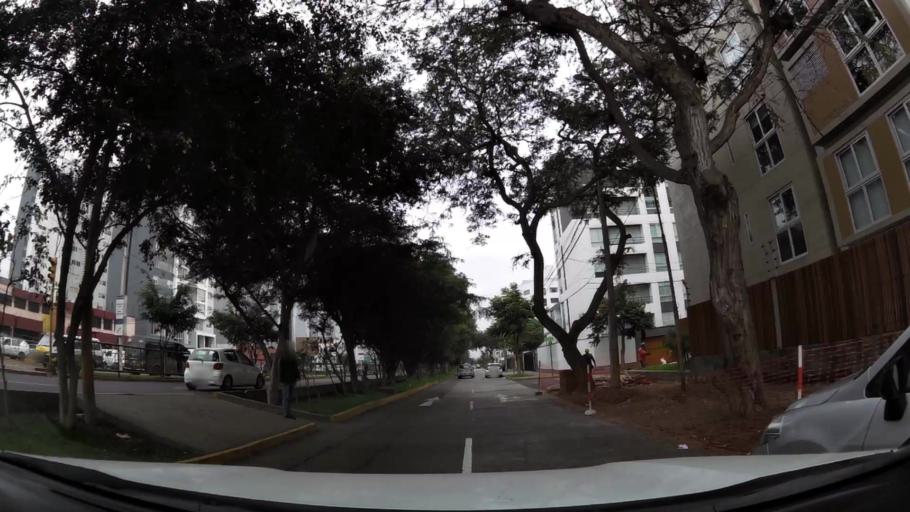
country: PE
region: Lima
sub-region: Lima
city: Surco
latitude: -12.1183
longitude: -77.0086
